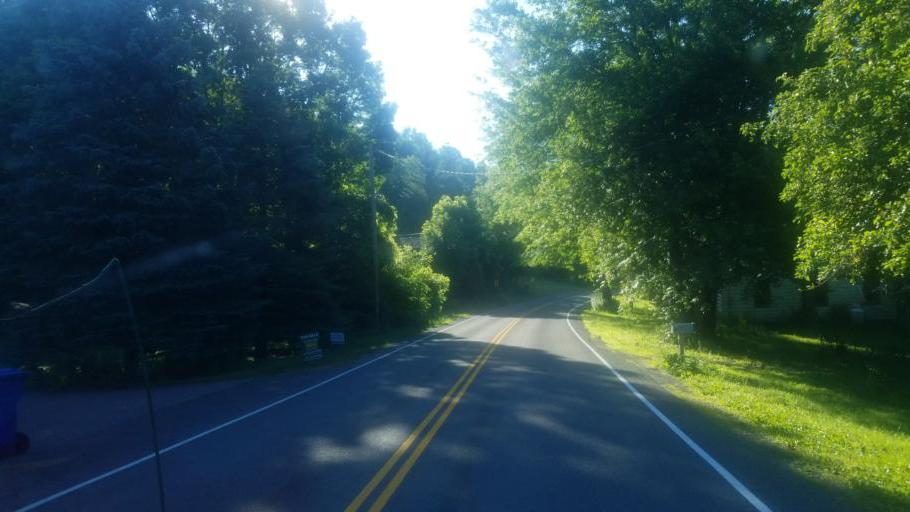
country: US
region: New York
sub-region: Wayne County
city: Lyons
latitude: 43.0885
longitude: -77.0396
